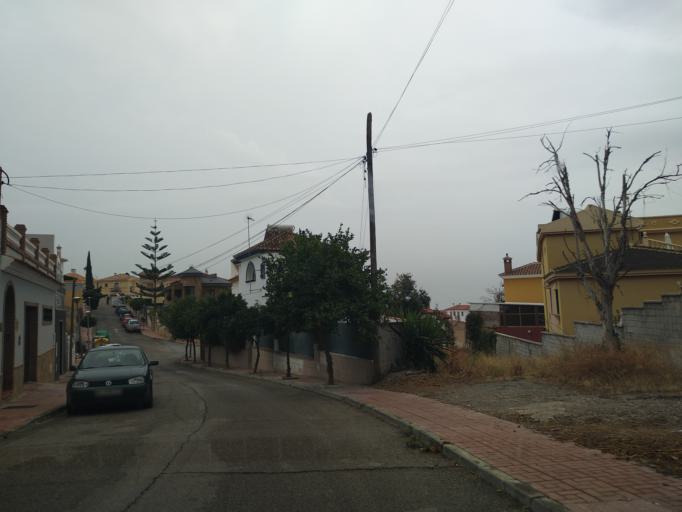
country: ES
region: Andalusia
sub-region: Provincia de Malaga
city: Malaga
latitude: 36.7453
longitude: -4.4748
